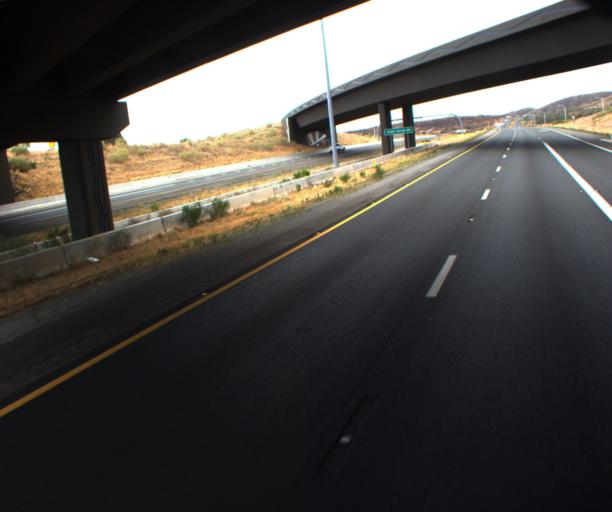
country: US
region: Arizona
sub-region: Yavapai County
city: Cordes Lakes
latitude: 34.3296
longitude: -112.1211
